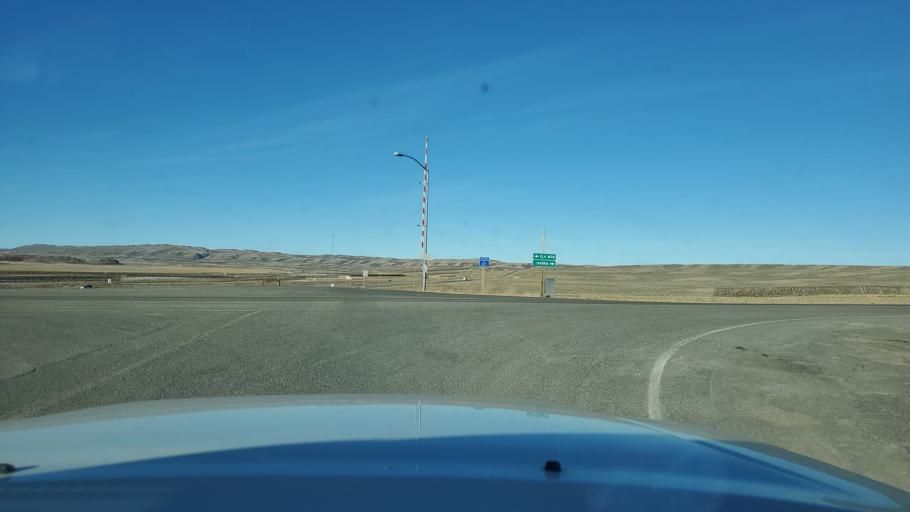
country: US
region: Wyoming
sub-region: Carbon County
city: Saratoga
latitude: 41.7258
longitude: -106.4596
